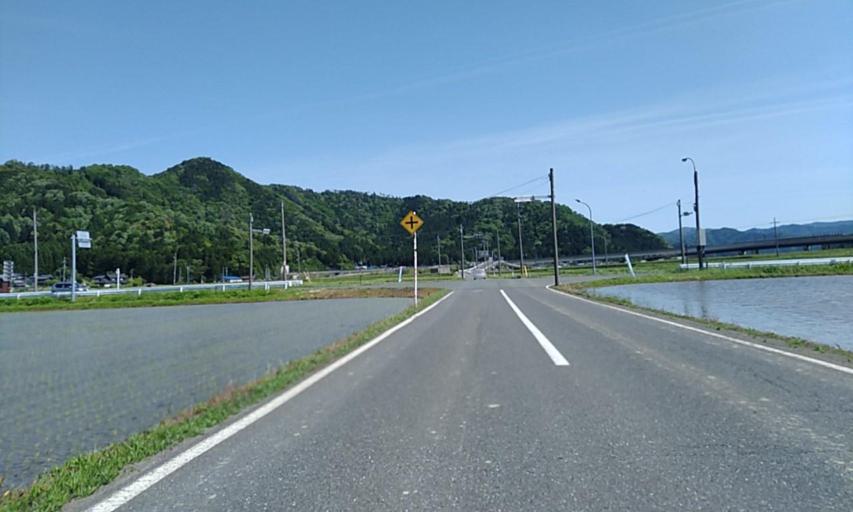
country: JP
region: Fukui
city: Obama
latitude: 35.5168
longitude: 135.8653
